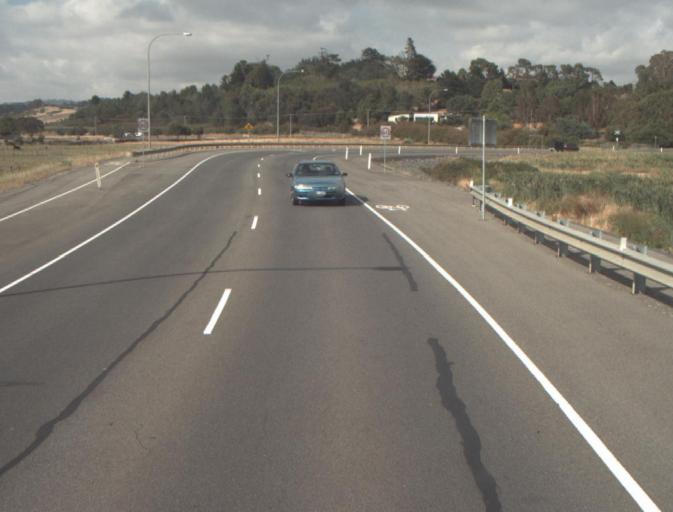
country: AU
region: Tasmania
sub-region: Launceston
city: Newstead
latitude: -41.4634
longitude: 147.1880
